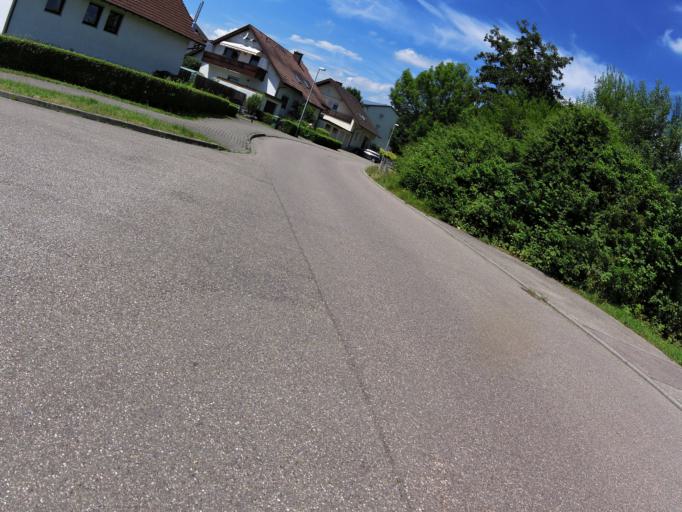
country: DE
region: Baden-Wuerttemberg
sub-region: Freiburg Region
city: Kippenheim
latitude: 48.3210
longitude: 7.8088
